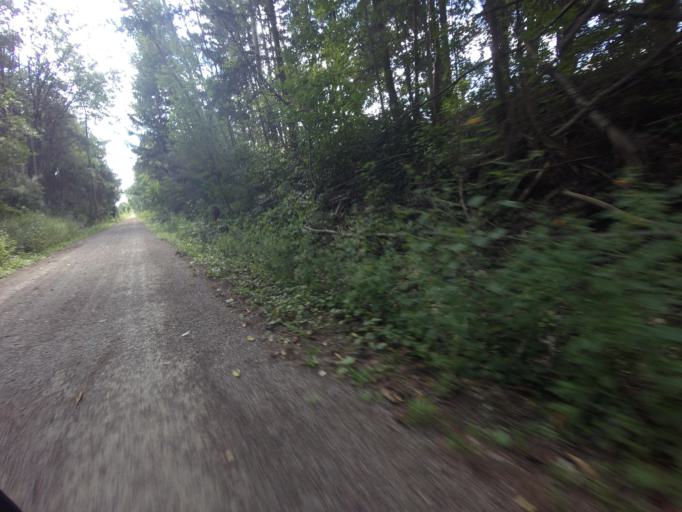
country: CA
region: Ontario
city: Huron East
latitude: 43.7237
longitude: -81.4053
